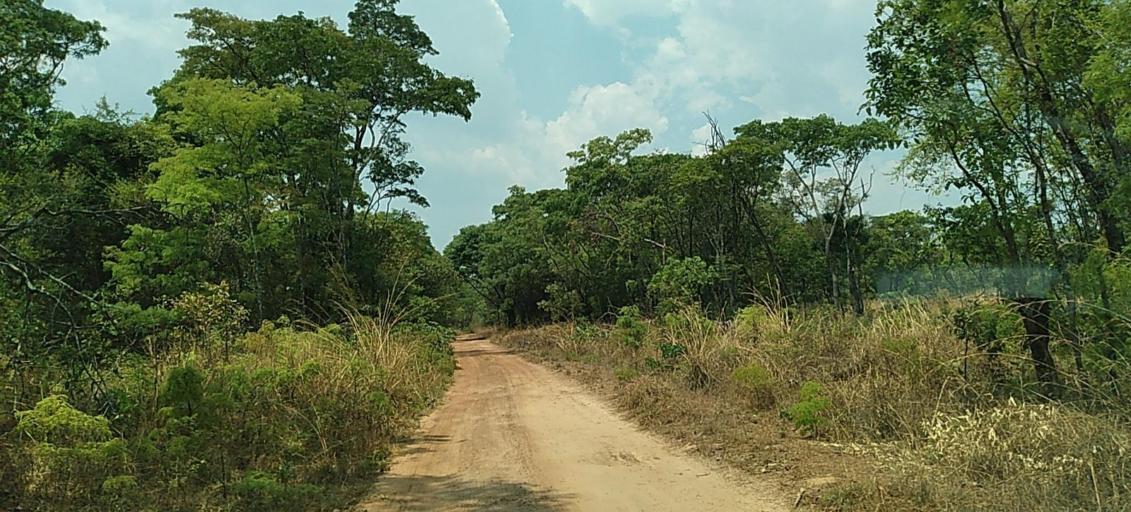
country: ZM
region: Copperbelt
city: Chingola
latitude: -12.7870
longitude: 27.6621
